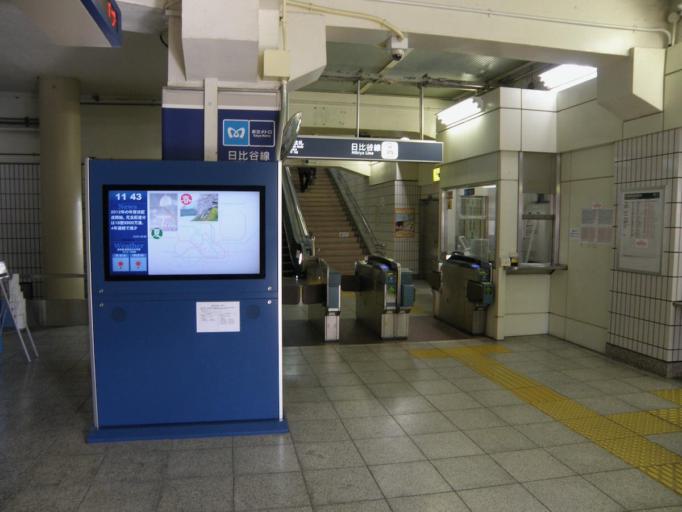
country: JP
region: Saitama
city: Soka
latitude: 35.7319
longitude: 139.7986
